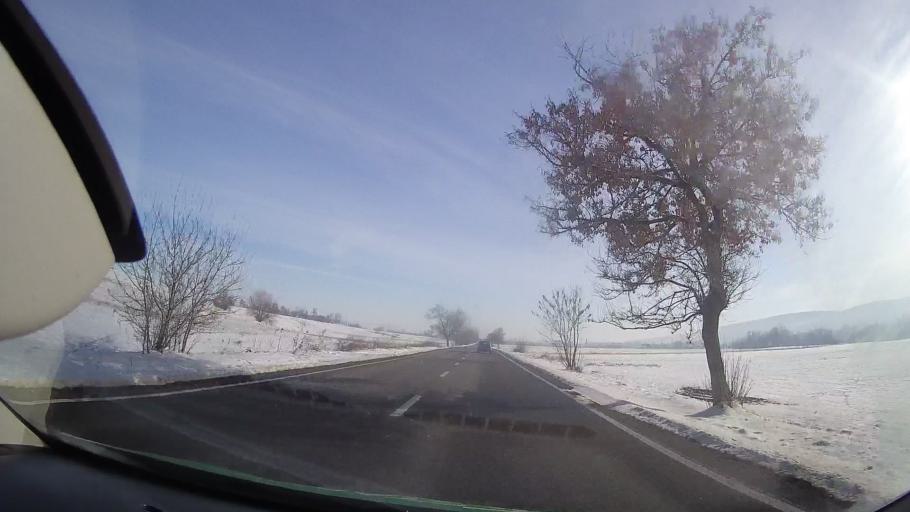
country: RO
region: Neamt
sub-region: Comuna Negresti
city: Negresti
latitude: 47.0660
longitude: 26.3737
